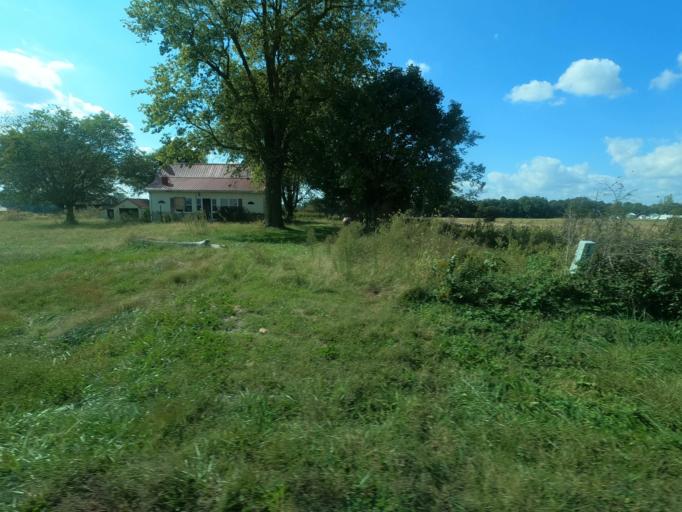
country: US
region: Illinois
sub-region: Massac County
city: Metropolis
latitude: 37.2122
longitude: -88.7292
